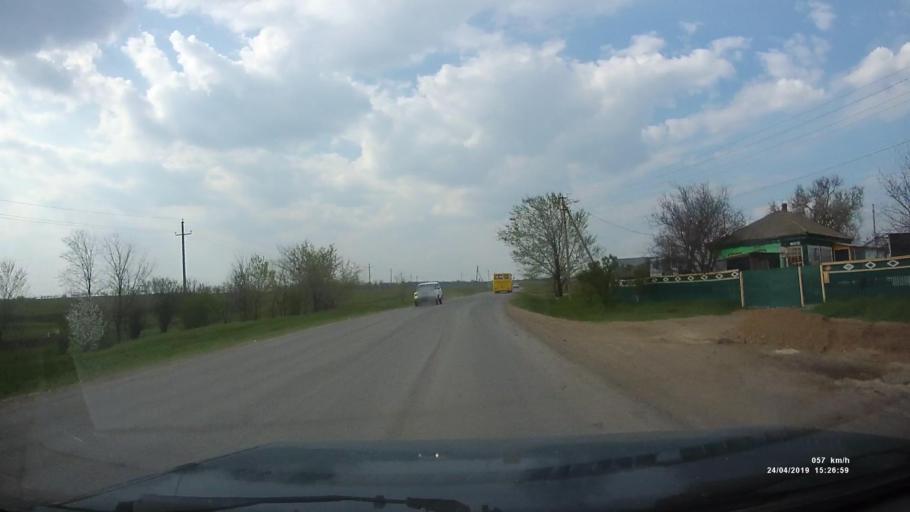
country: RU
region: Rostov
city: Remontnoye
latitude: 46.5606
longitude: 43.0295
